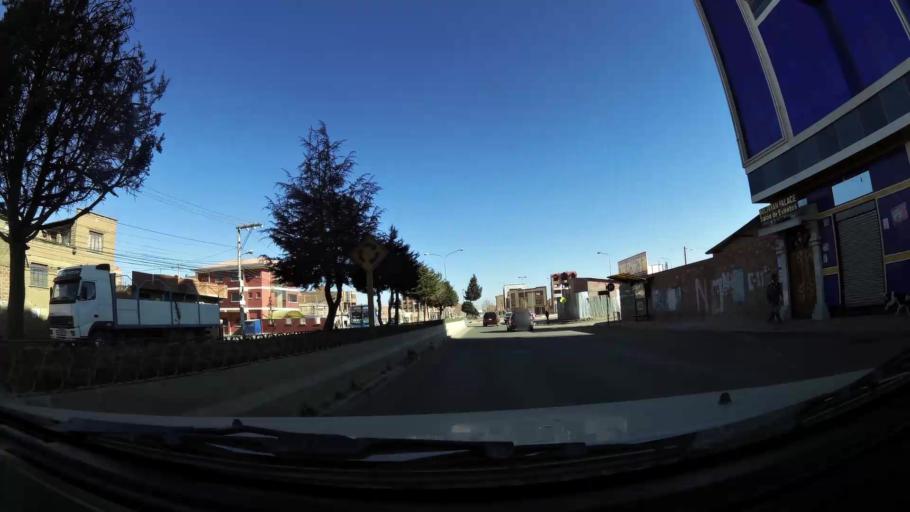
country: BO
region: La Paz
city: La Paz
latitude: -16.5387
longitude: -68.1849
